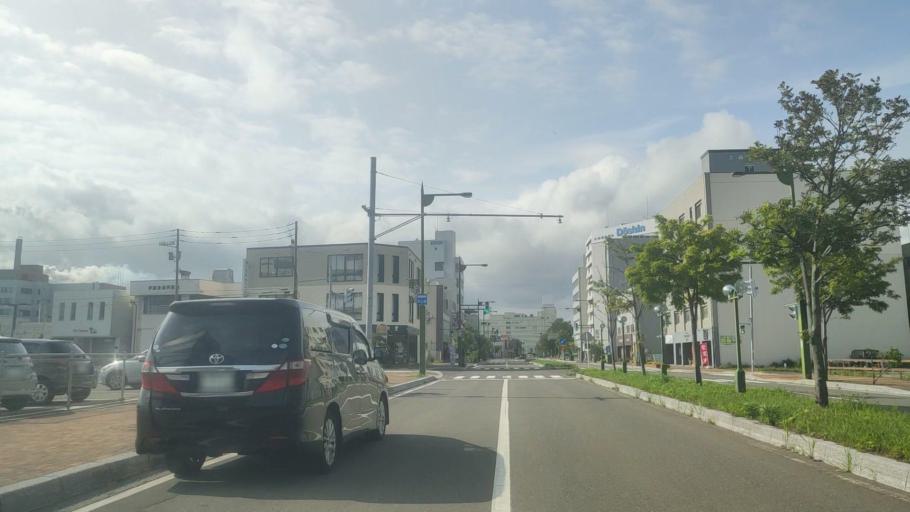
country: JP
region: Hokkaido
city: Tomakomai
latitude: 42.6339
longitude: 141.6019
